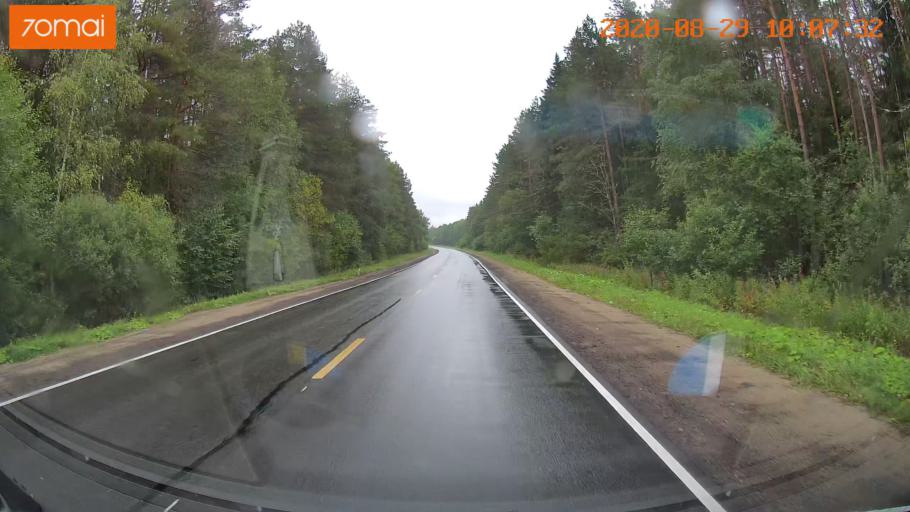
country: RU
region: Ivanovo
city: Kuznechikha
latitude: 57.3801
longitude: 42.5690
